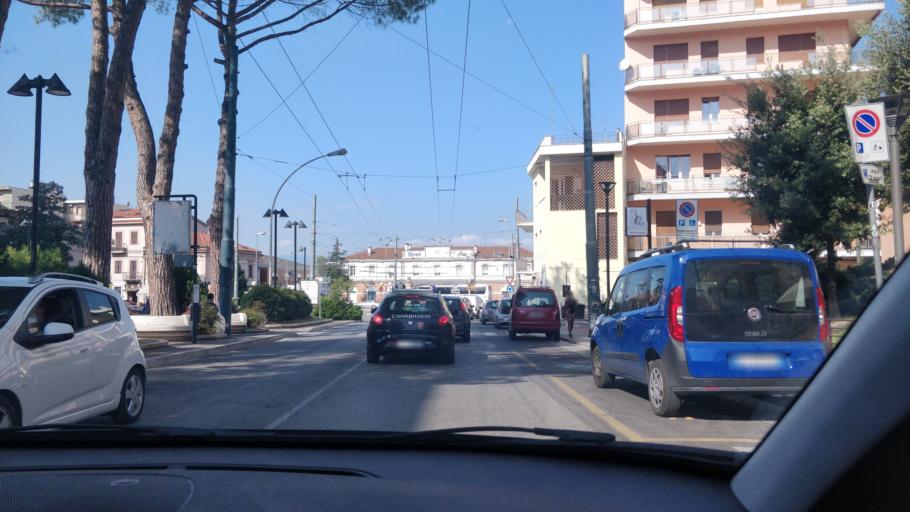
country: IT
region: Abruzzo
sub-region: Provincia di Chieti
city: Chieti
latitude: 42.3569
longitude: 14.1398
